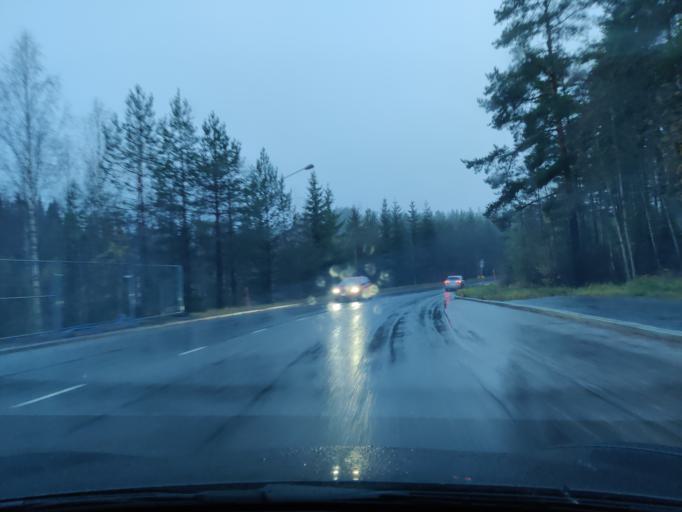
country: FI
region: Northern Savo
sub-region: Kuopio
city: Kuopio
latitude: 62.8448
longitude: 27.6535
